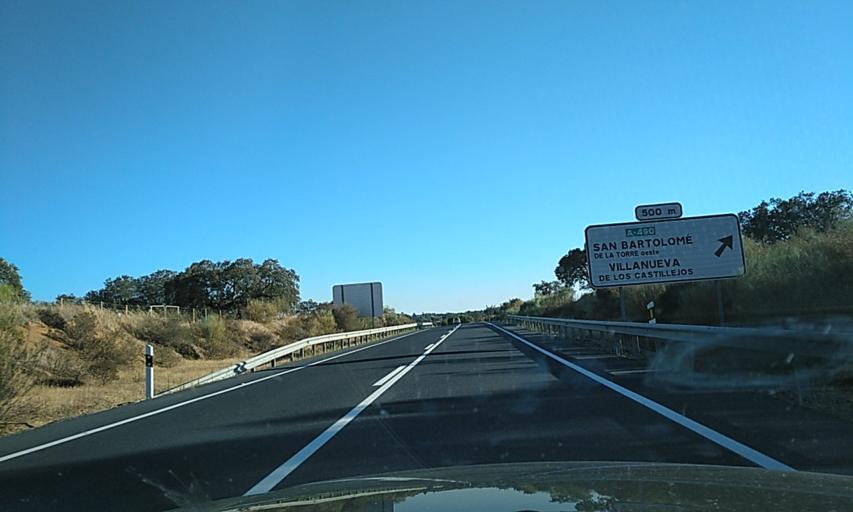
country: ES
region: Andalusia
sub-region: Provincia de Huelva
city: San Bartolome de la Torre
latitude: 37.4550
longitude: -7.1267
